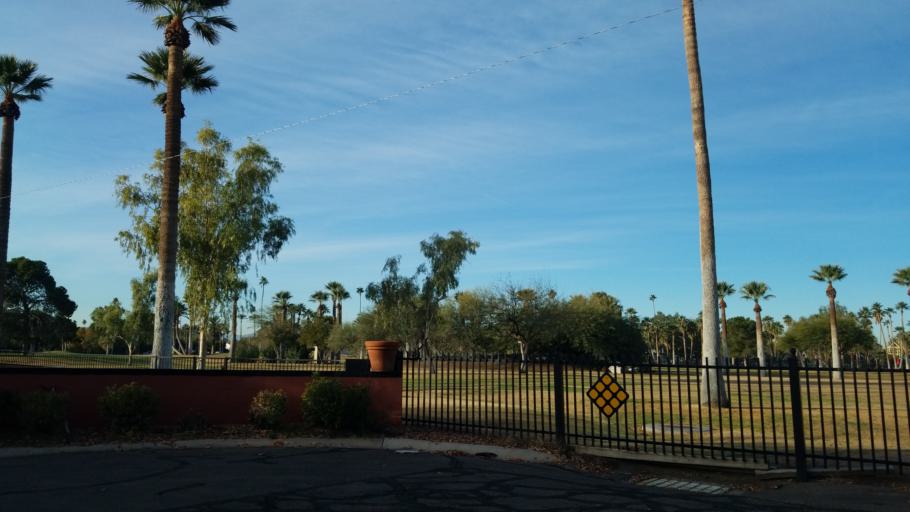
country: US
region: Arizona
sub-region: Maricopa County
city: Phoenix
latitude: 33.4750
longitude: -112.0845
